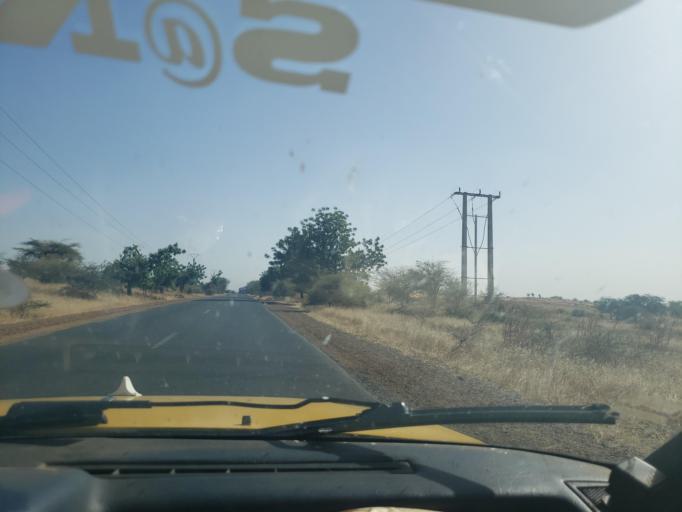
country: SN
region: Louga
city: Louga
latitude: 15.6532
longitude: -16.2557
